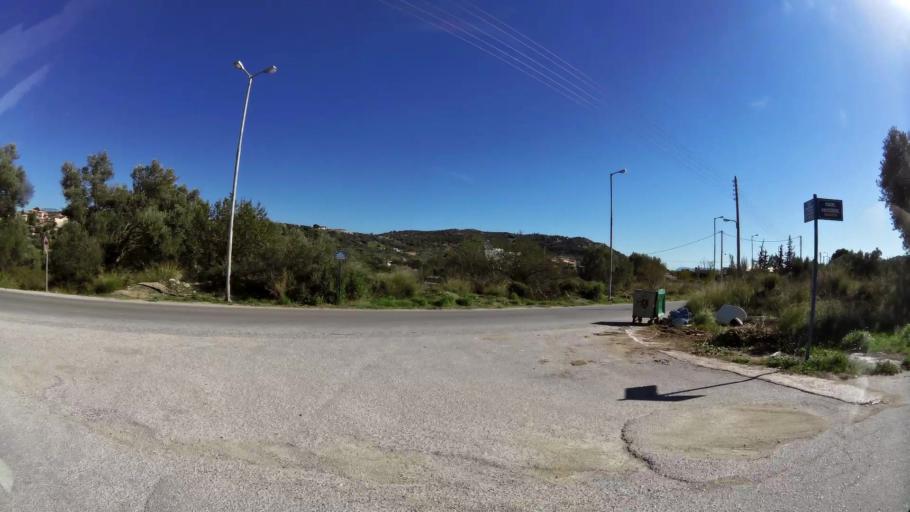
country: GR
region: Attica
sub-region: Nomarchia Anatolikis Attikis
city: Paiania
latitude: 37.9700
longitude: 23.8623
